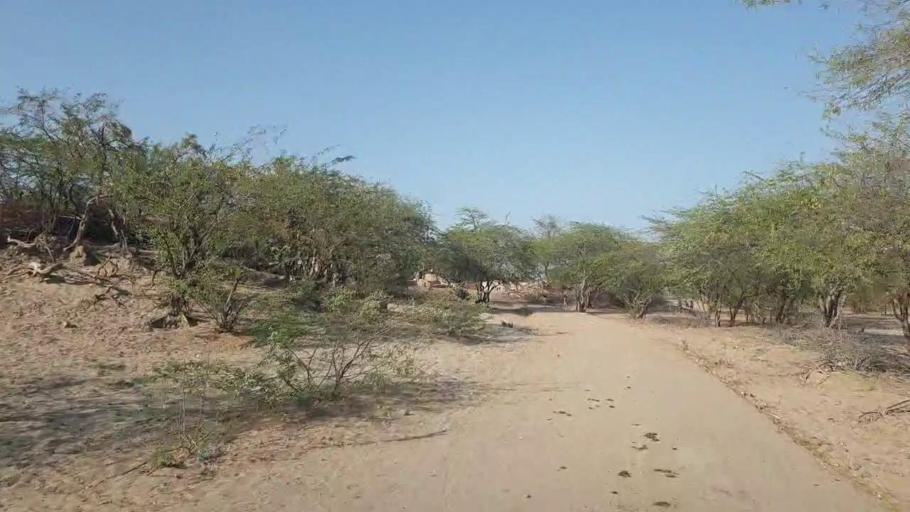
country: PK
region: Sindh
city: Chor
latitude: 25.5377
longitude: 69.6998
